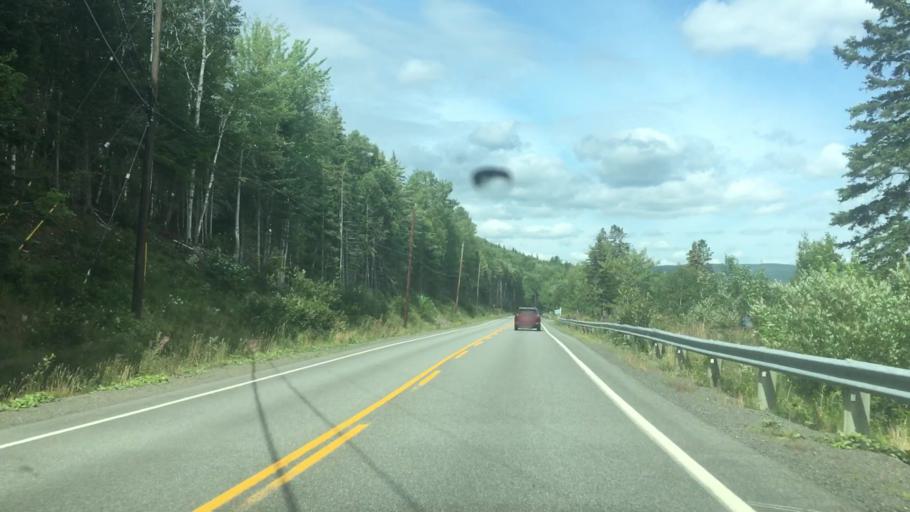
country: CA
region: Nova Scotia
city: Sydney Mines
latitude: 46.2737
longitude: -60.6103
